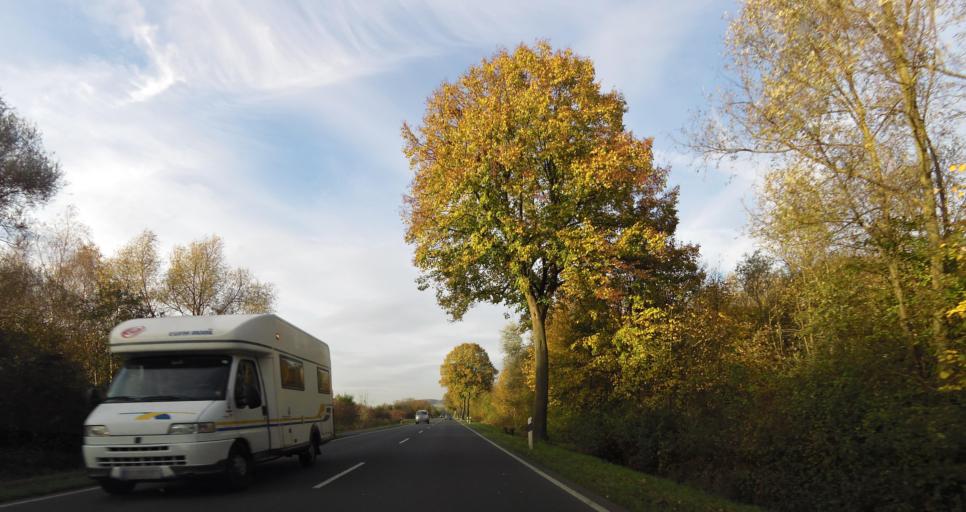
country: DE
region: Lower Saxony
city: Northeim
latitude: 51.7433
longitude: 9.9694
